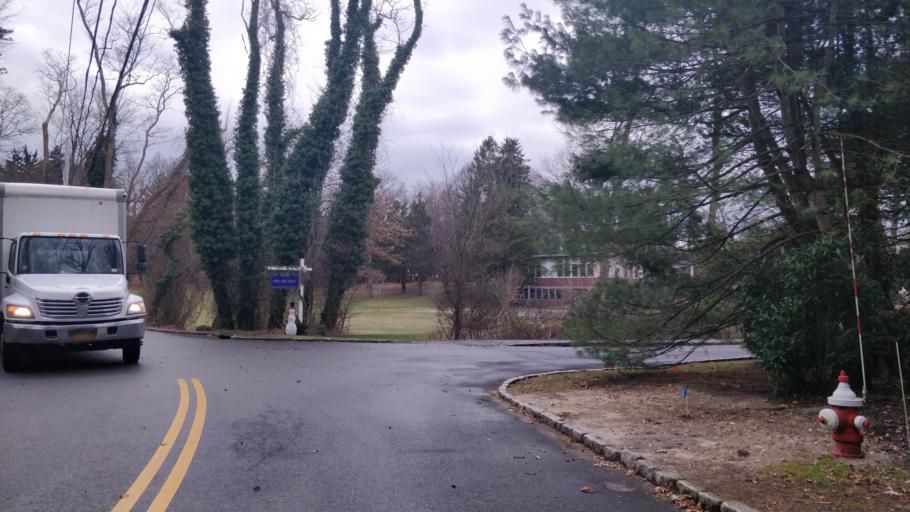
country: US
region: New York
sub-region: Nassau County
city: Laurel Hollow
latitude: 40.8548
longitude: -73.4752
